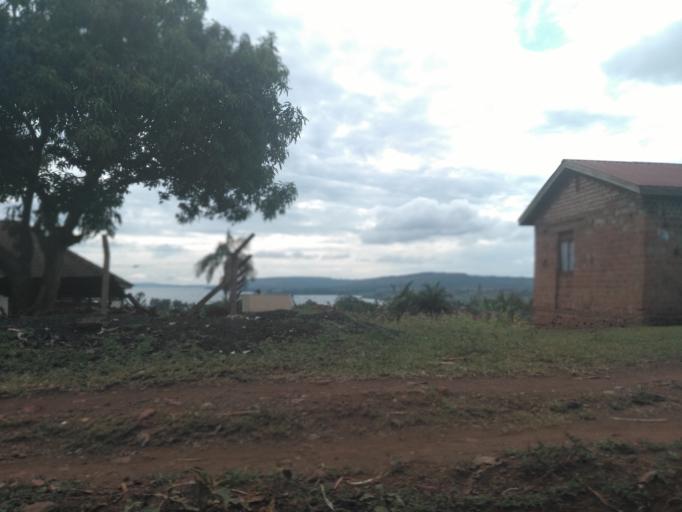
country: UG
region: Central Region
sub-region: Buikwe District
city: Njeru
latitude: 0.4160
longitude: 33.1838
